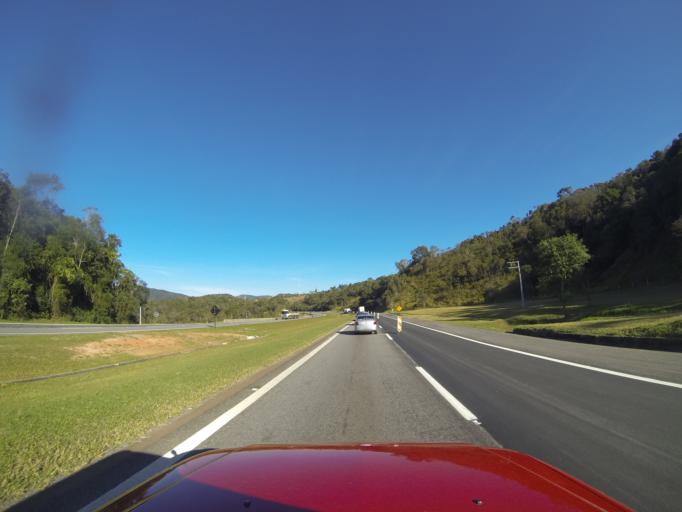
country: BR
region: Sao Paulo
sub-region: Bom Jesus Dos Perdoes
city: Bom Jesus dos Perdoes
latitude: -23.1870
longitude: -46.3600
